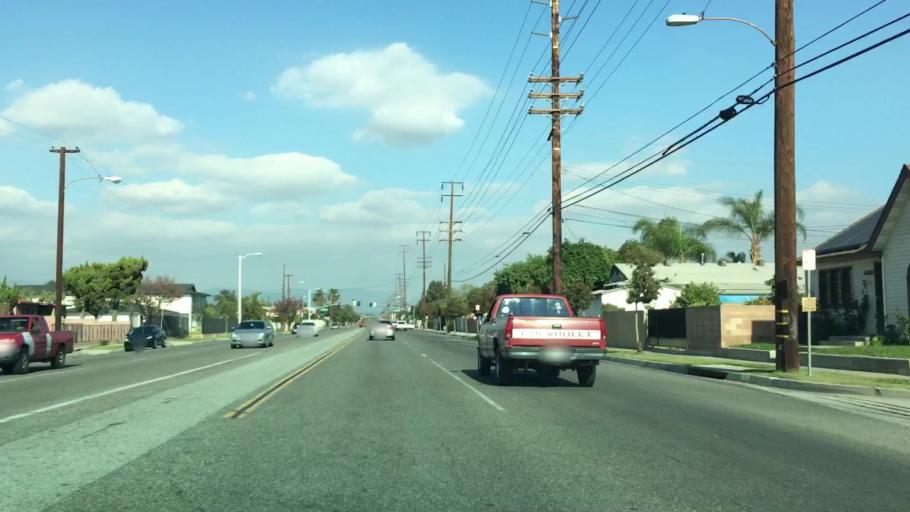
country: US
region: California
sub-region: Los Angeles County
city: West Puente Valley
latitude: 34.0389
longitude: -117.9700
